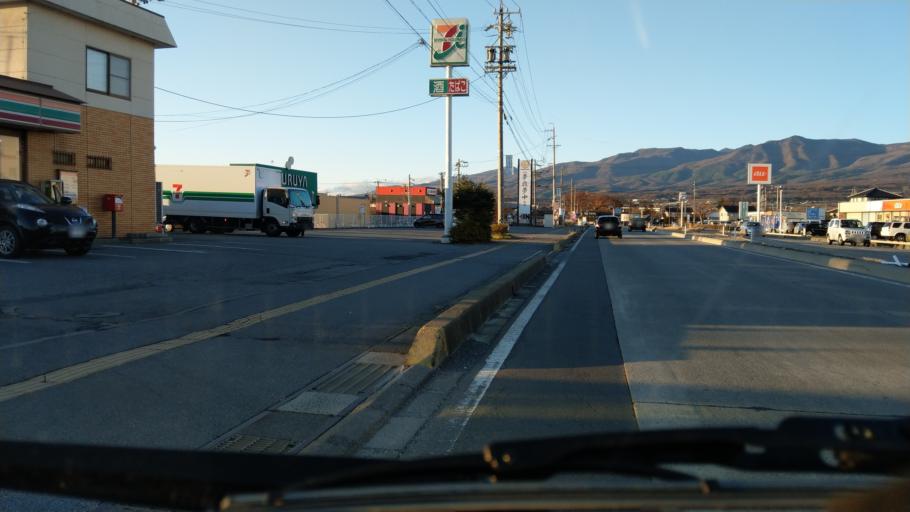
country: JP
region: Nagano
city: Komoro
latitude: 36.2976
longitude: 138.4682
